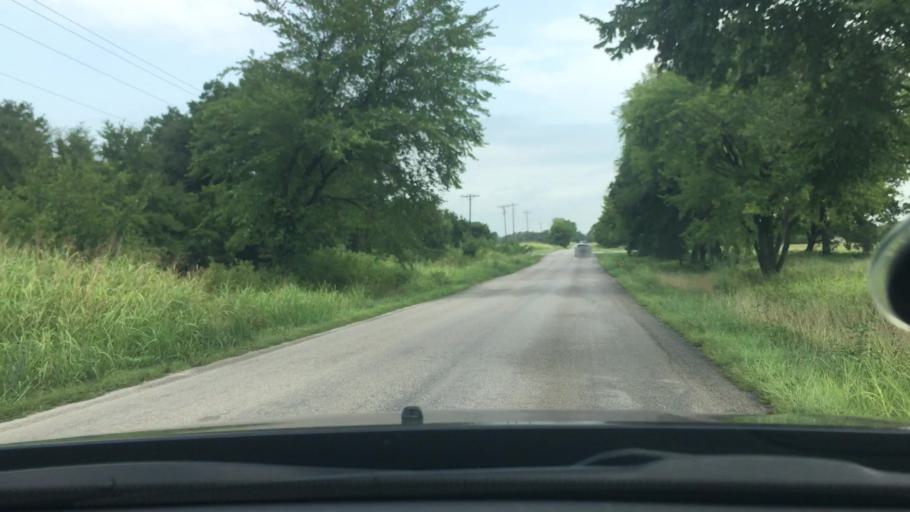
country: US
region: Oklahoma
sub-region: Carter County
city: Lone Grove
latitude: 34.2039
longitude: -97.2650
